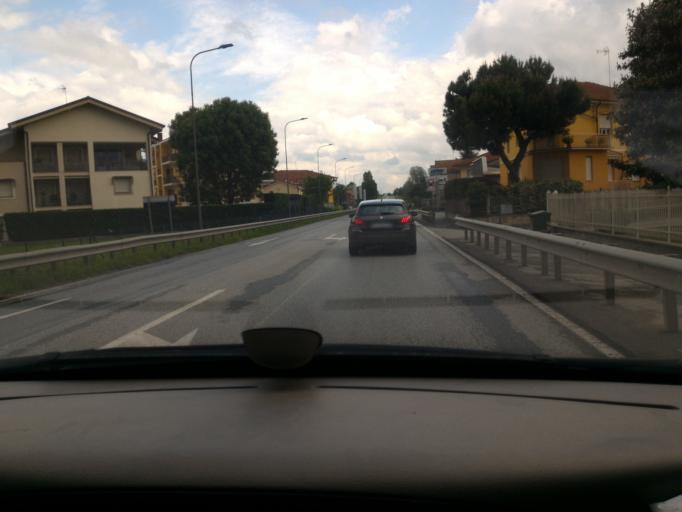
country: IT
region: Piedmont
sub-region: Provincia di Cuneo
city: Savigliano
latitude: 44.6397
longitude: 7.6562
